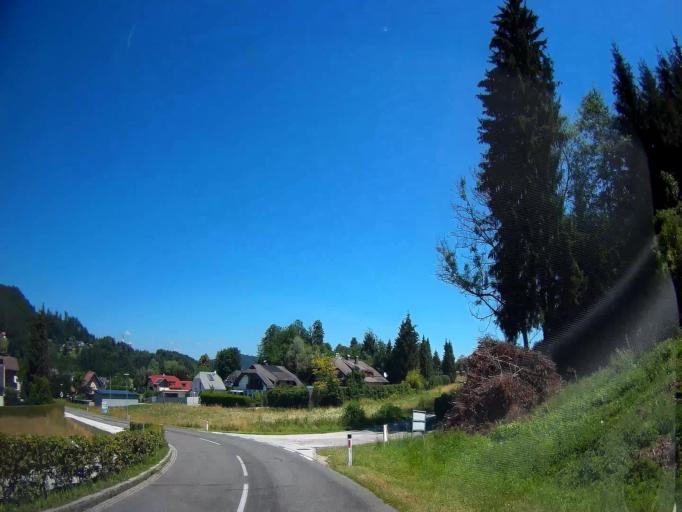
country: AT
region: Carinthia
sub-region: Politischer Bezirk Klagenfurt Land
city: Keutschach am See
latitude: 46.5988
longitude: 14.1745
